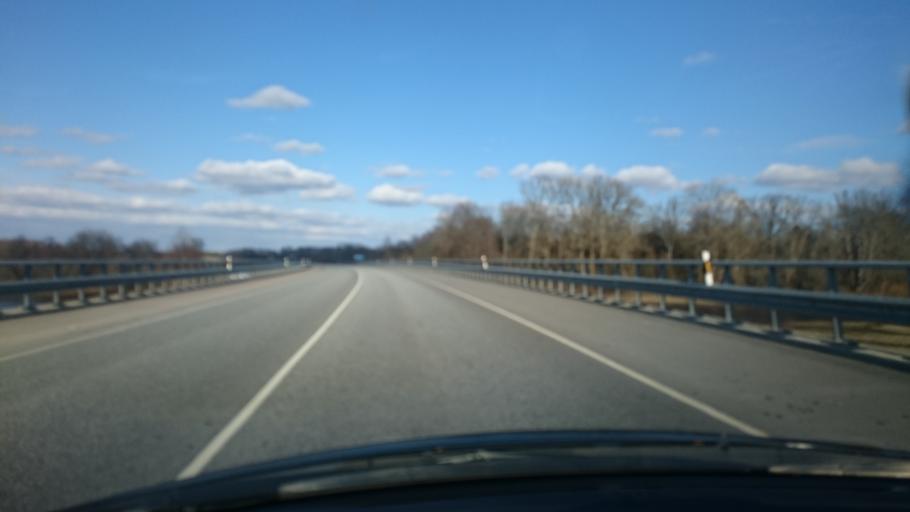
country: EE
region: Laeaene
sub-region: Lihula vald
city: Lihula
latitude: 58.7333
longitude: 23.9878
